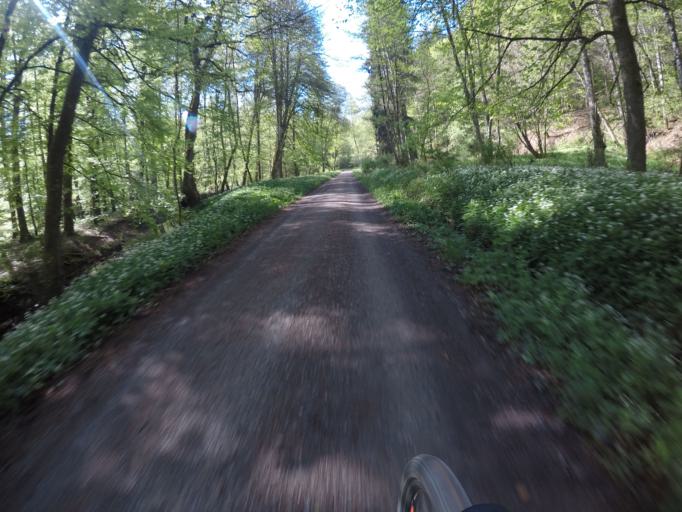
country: DE
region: Baden-Wuerttemberg
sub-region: Tuebingen Region
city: Dettenhausen
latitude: 48.5633
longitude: 9.0933
